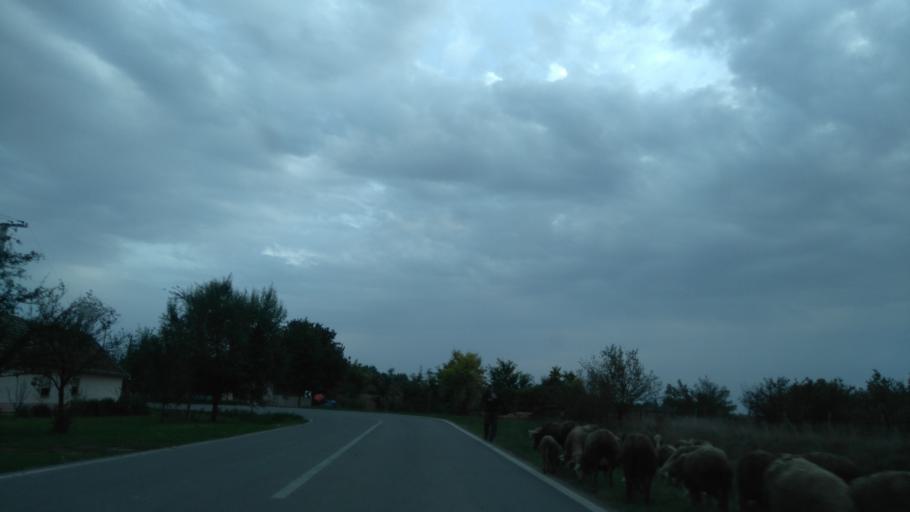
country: RS
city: Mol
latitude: 45.7545
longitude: 20.1253
